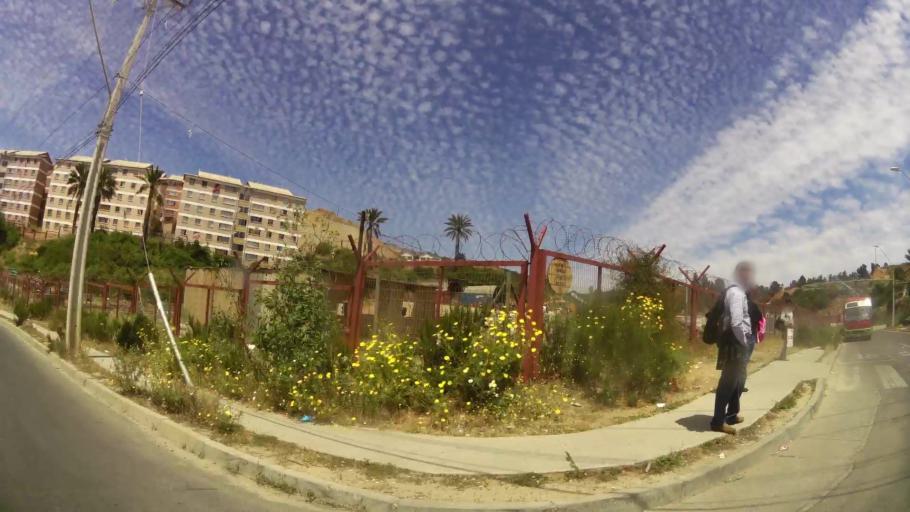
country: CL
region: Valparaiso
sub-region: Provincia de Valparaiso
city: Vina del Mar
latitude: -33.0623
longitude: -71.5627
